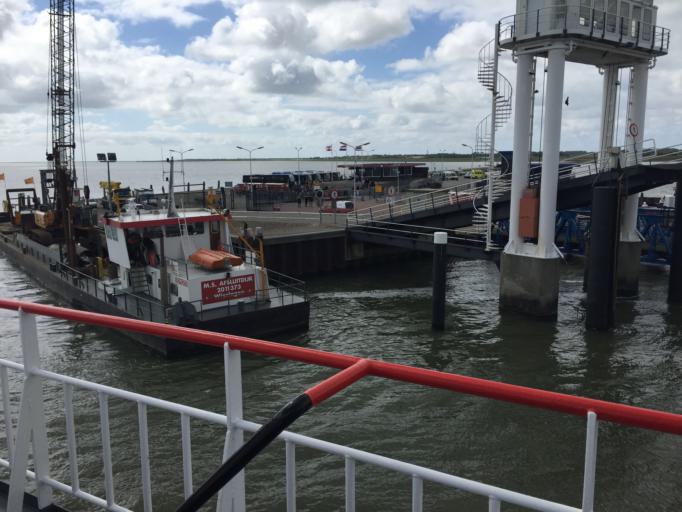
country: NL
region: Friesland
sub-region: Gemeente Schiermonnikoog
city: Schiermonnikoog
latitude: 53.4684
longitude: 6.2035
